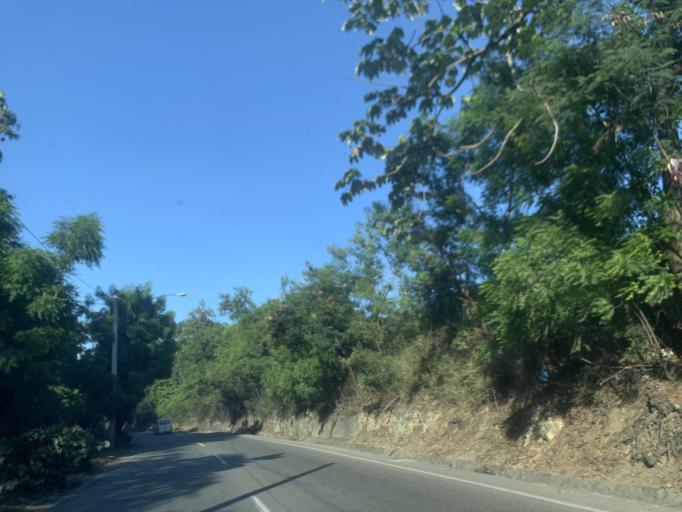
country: DO
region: San Cristobal
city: El Carril
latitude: 18.4332
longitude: -70.0222
